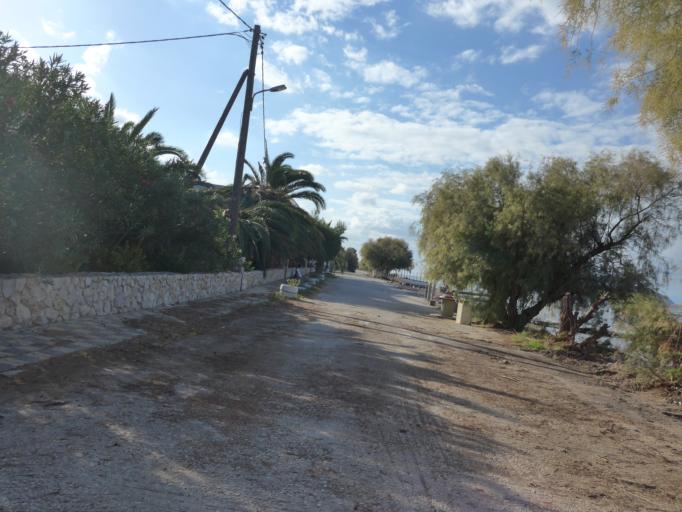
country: GR
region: Peloponnese
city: Asklipieio
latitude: 37.4923
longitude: 22.9910
